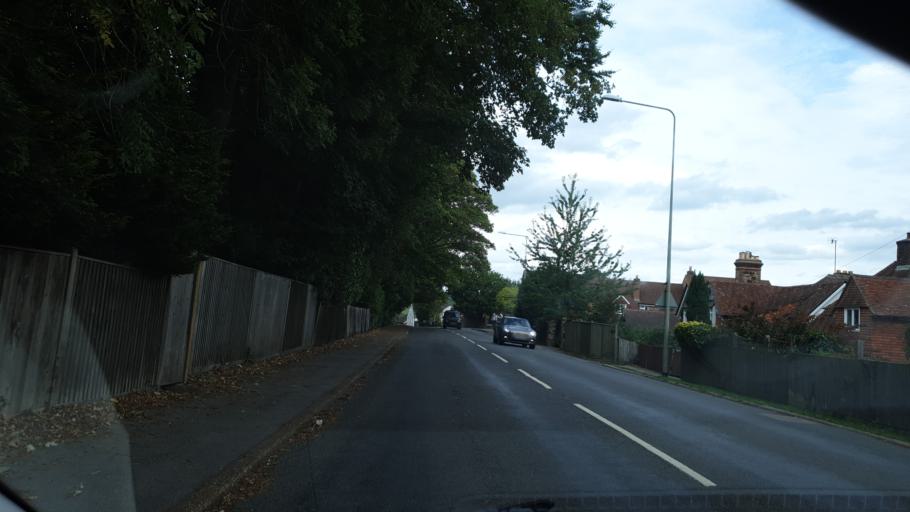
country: GB
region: England
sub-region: East Sussex
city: Forest Row
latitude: 51.0941
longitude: 0.0331
